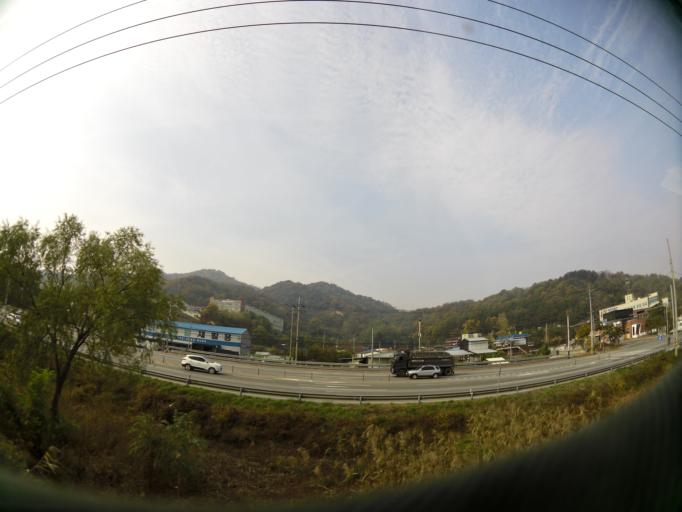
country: KR
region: Gyeongsangbuk-do
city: Waegwan
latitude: 36.0076
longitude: 128.3878
